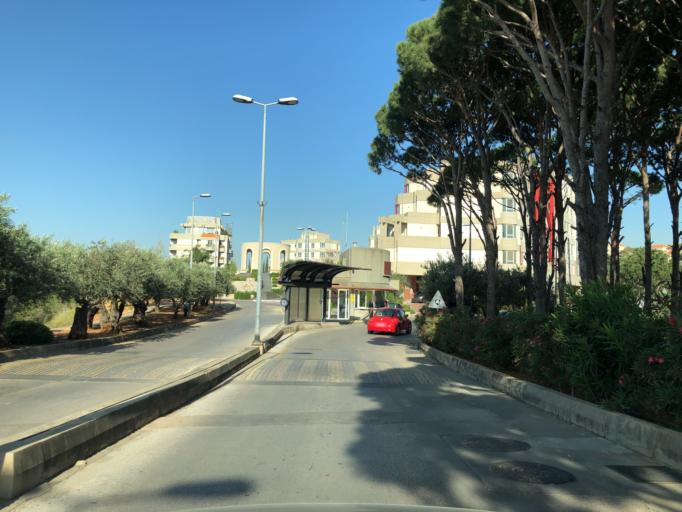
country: LB
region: Mont-Liban
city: Djounie
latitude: 33.9507
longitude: 35.6158
